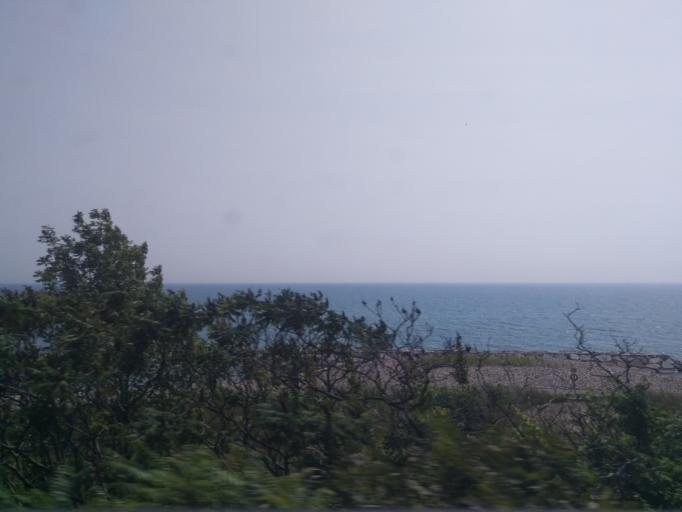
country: CA
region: Ontario
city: Ajax
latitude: 43.7893
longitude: -79.1219
